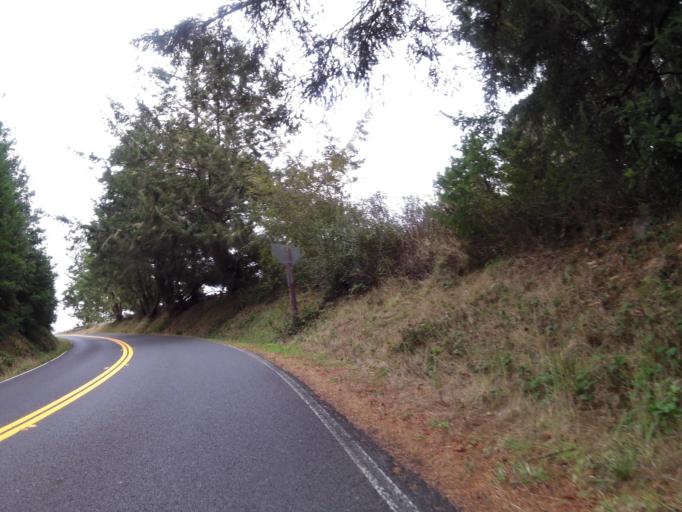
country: US
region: California
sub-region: Sonoma County
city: Monte Rio
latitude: 38.5154
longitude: -123.2412
